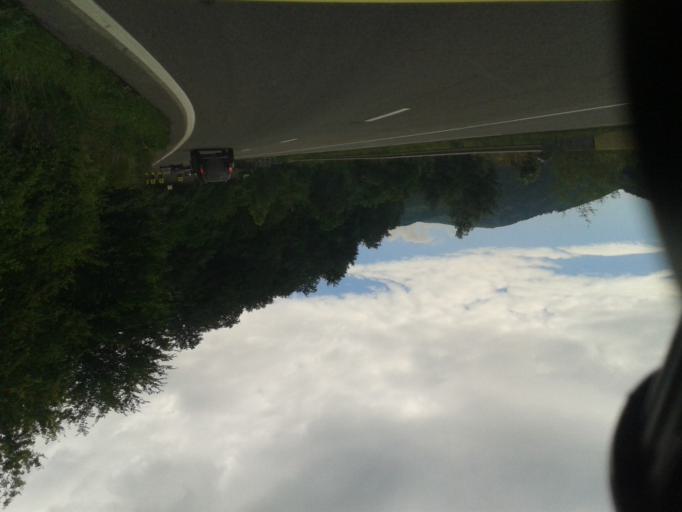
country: RO
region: Prahova
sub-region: Comuna Comarnic
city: Posada
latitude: 45.2715
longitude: 25.6225
